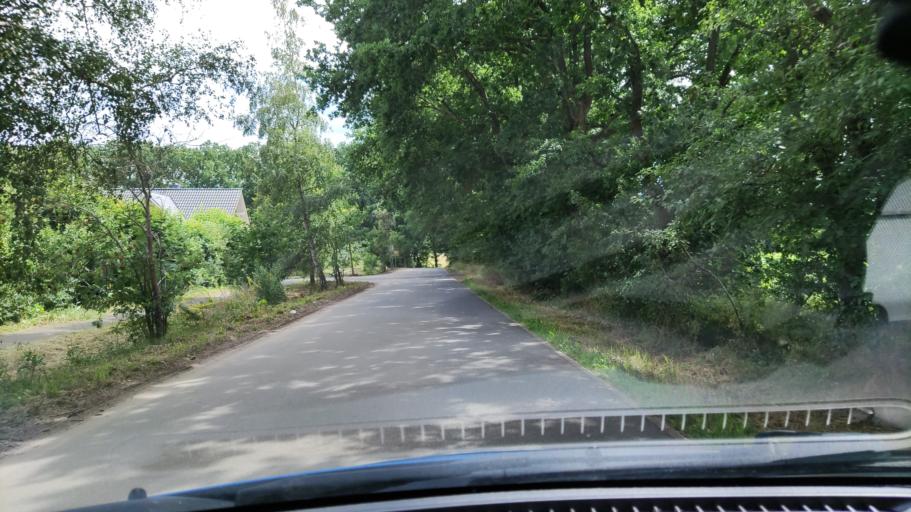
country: DE
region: Lower Saxony
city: Vogelsen
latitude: 53.2697
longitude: 10.3530
